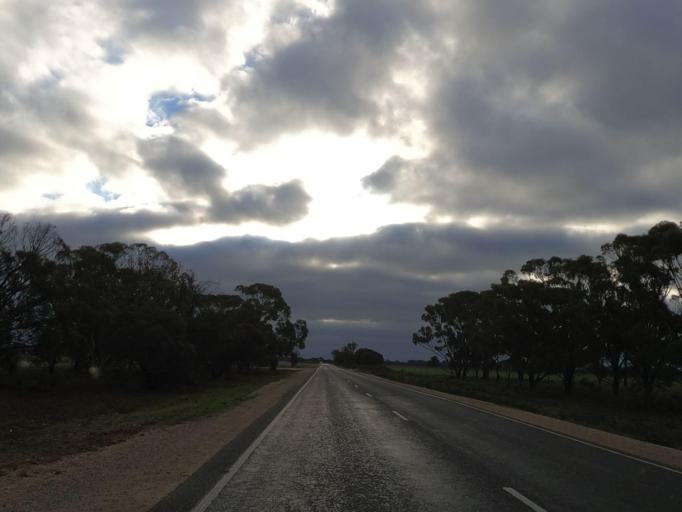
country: AU
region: Victoria
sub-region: Swan Hill
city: Swan Hill
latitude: -35.6562
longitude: 143.8513
